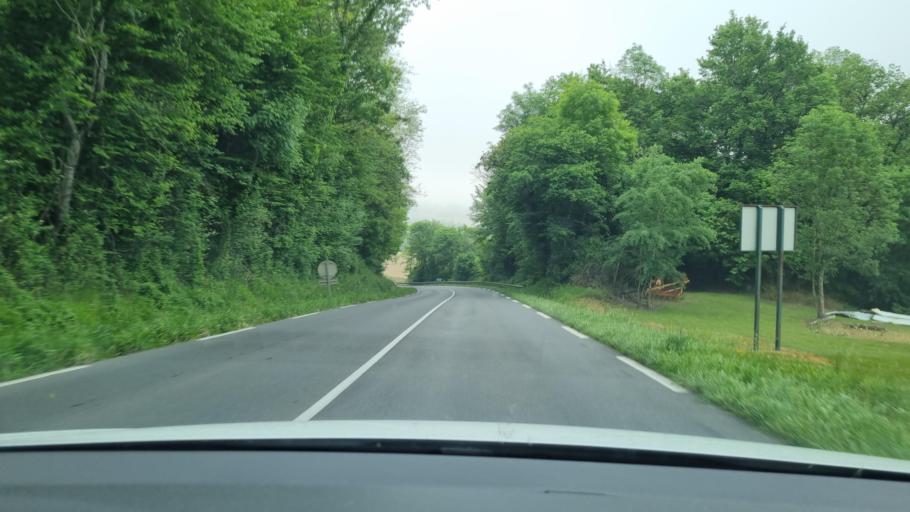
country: FR
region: Aquitaine
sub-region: Departement des Landes
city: Hagetmau
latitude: 43.5965
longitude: -0.6465
